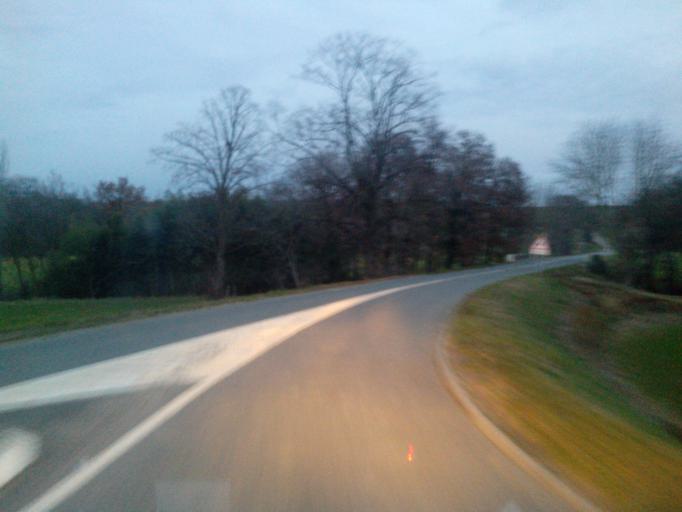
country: FR
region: Midi-Pyrenees
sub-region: Departement de la Haute-Garonne
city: Avignonet-Lauragais
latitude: 43.2799
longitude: 1.7942
